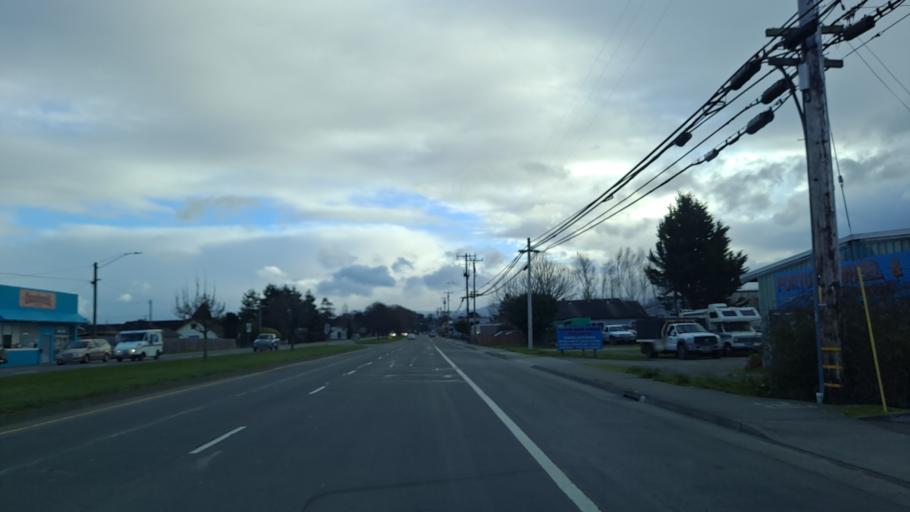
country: US
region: California
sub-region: Humboldt County
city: Fortuna
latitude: 40.5882
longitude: -124.1469
